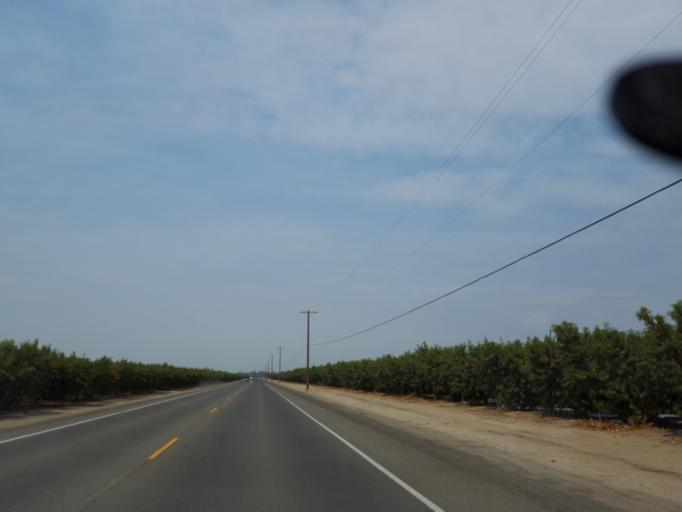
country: US
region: California
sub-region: Fresno County
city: Minkler
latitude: 36.6988
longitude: -119.4575
